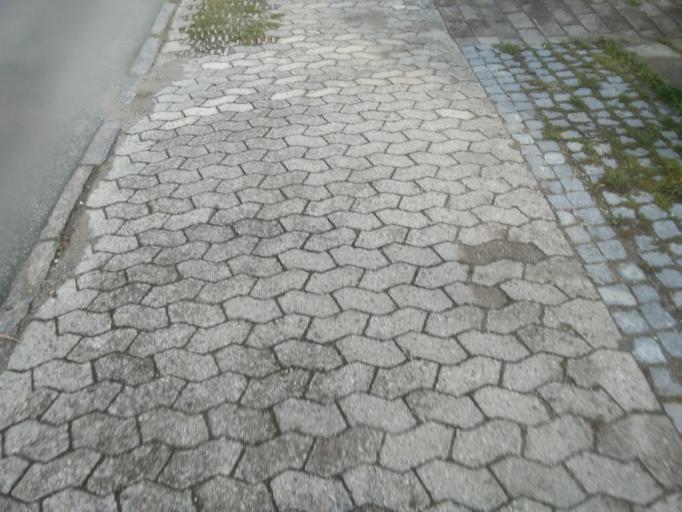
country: DK
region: Capital Region
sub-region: Gladsaxe Municipality
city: Buddinge
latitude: 55.7251
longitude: 12.5045
